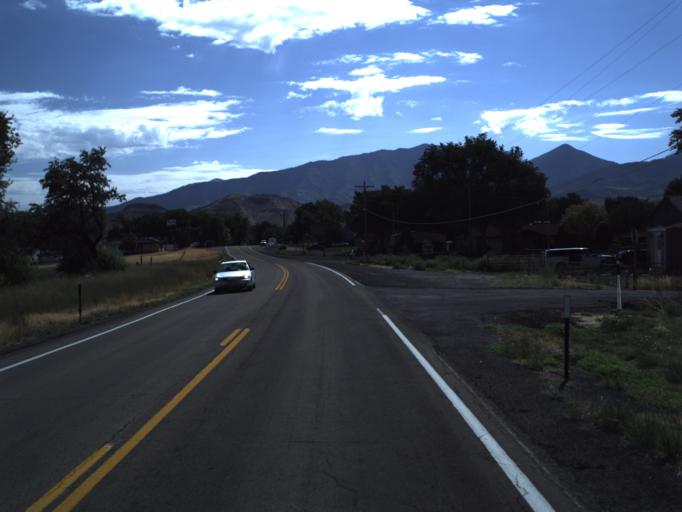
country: US
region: Utah
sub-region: Utah County
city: Genola
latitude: 39.9525
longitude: -111.9076
